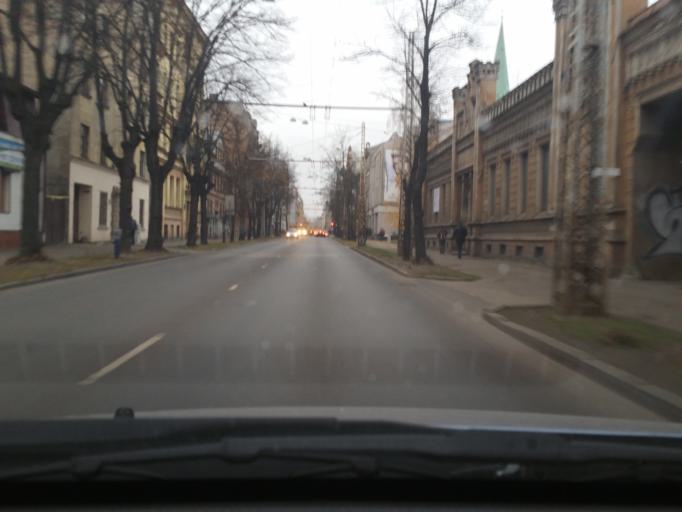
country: LV
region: Riga
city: Riga
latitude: 56.9646
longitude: 24.1347
